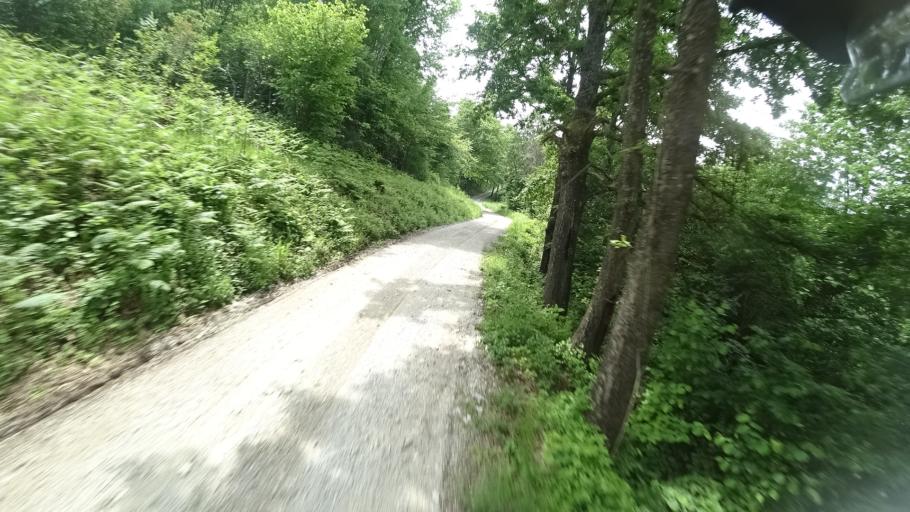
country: HR
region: Karlovacka
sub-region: Grad Karlovac
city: Slunj
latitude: 45.1891
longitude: 15.6257
